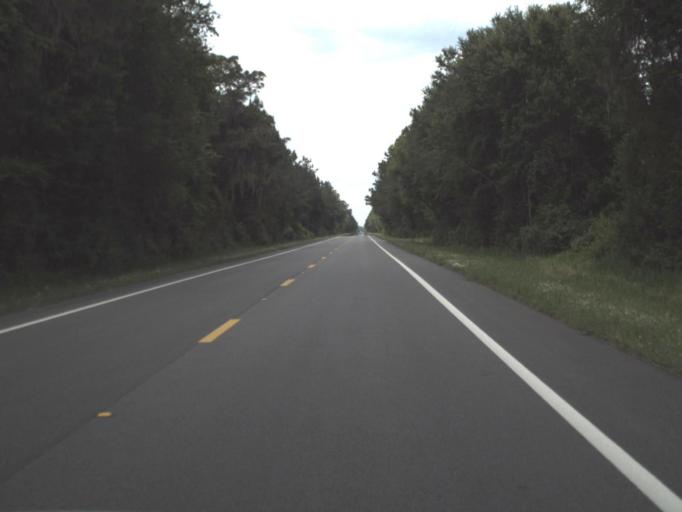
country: US
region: Florida
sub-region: Hamilton County
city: Jasper
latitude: 30.5597
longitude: -82.6806
